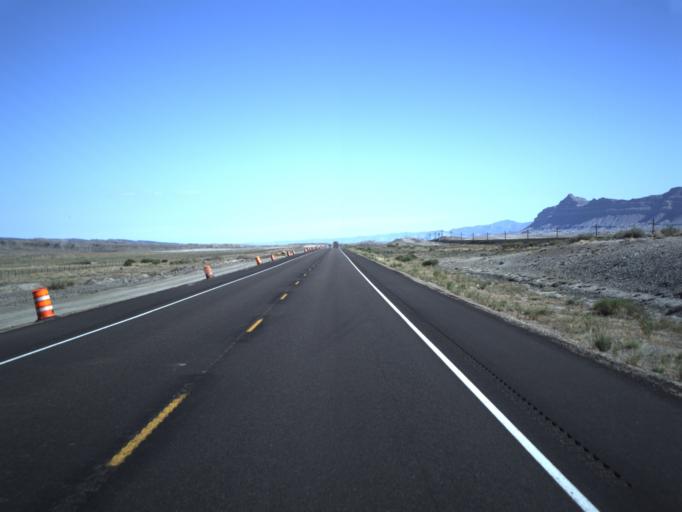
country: US
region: Utah
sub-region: Carbon County
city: East Carbon City
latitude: 39.0492
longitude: -110.3098
